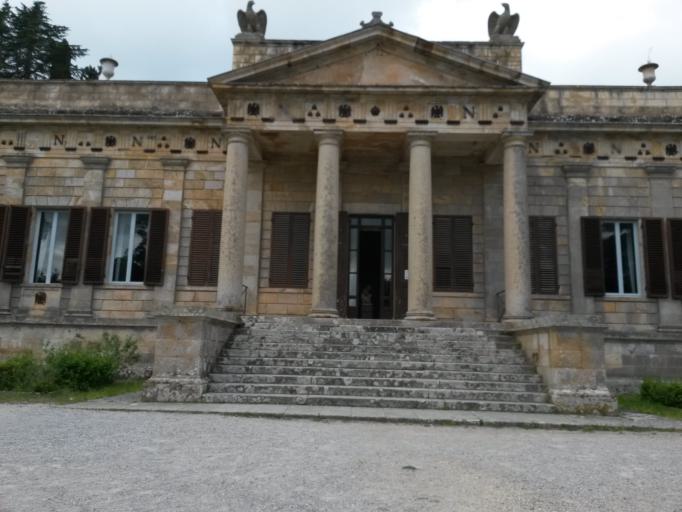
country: IT
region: Tuscany
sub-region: Provincia di Livorno
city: Portoferraio
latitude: 42.7858
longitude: 10.2809
